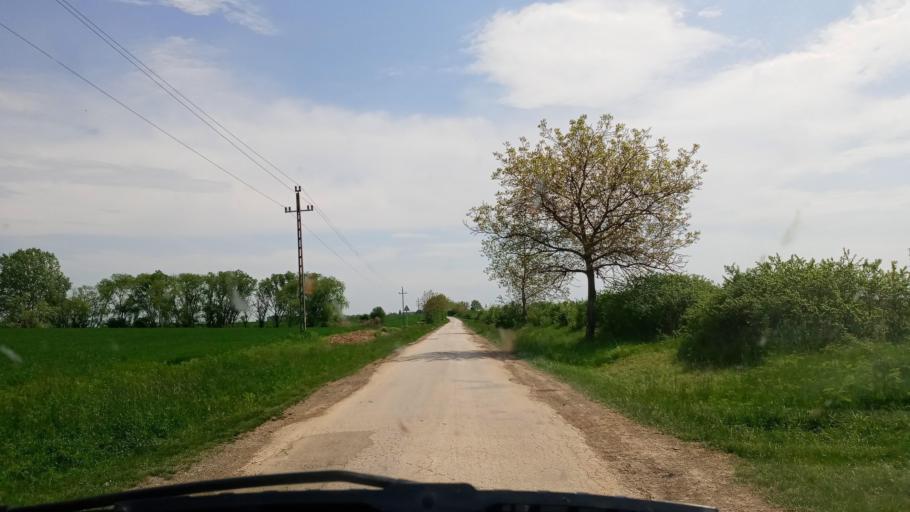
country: HU
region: Baranya
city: Villany
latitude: 45.8207
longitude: 18.5064
